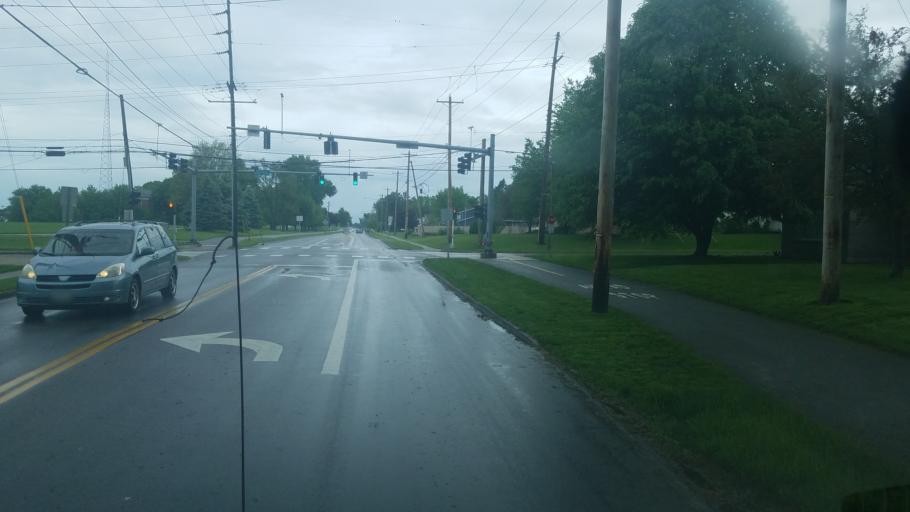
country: US
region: Ohio
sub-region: Wayne County
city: Wooster
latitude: 40.8282
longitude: -81.9388
